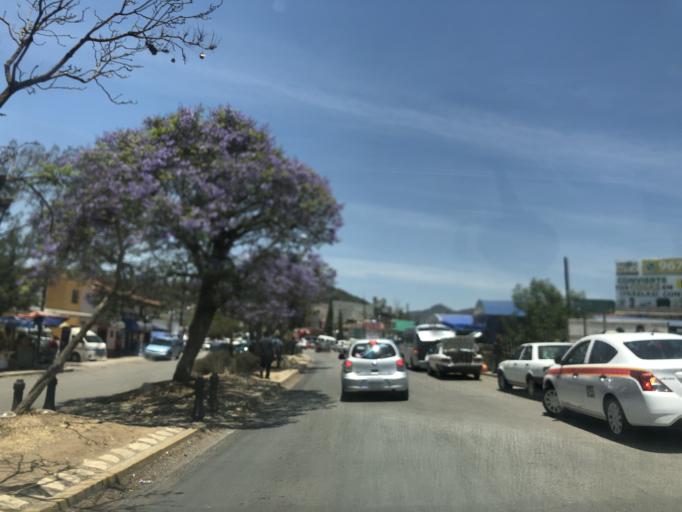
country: MX
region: Chiapas
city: San Cristobal de las Casas
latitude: 16.7289
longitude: -92.6365
